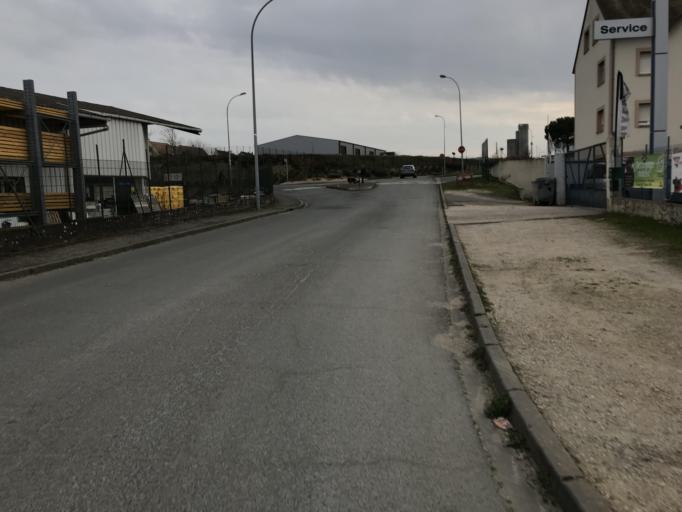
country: FR
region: Ile-de-France
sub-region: Departement de l'Essonne
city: Limours
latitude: 48.6456
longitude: 2.0638
